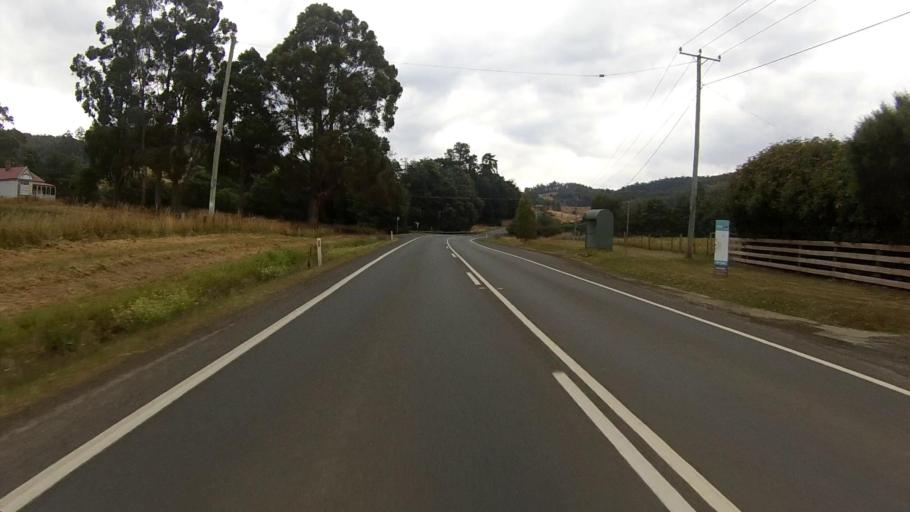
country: AU
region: Tasmania
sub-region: Huon Valley
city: Cygnet
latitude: -43.1373
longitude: 147.0556
